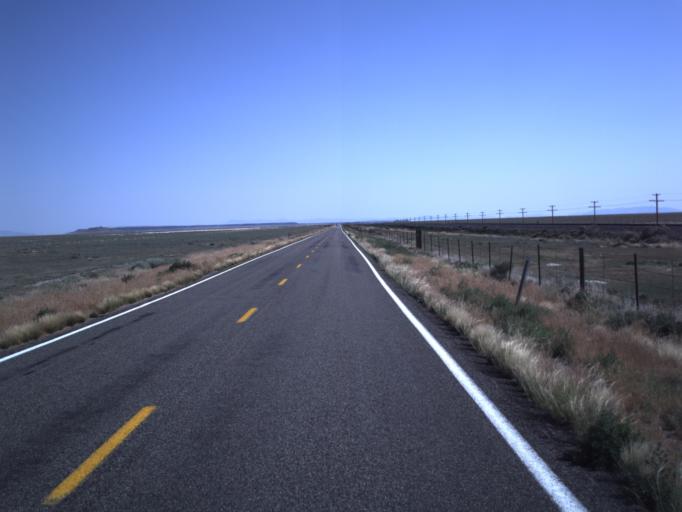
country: US
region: Utah
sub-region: Millard County
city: Delta
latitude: 39.0193
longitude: -112.7798
